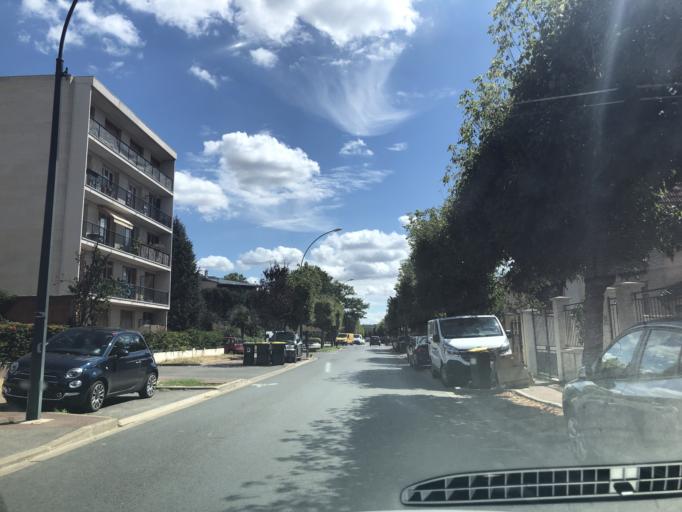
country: FR
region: Ile-de-France
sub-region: Departement du Val-de-Marne
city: Saint-Maur-des-Fosses
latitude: 48.7963
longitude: 2.4932
